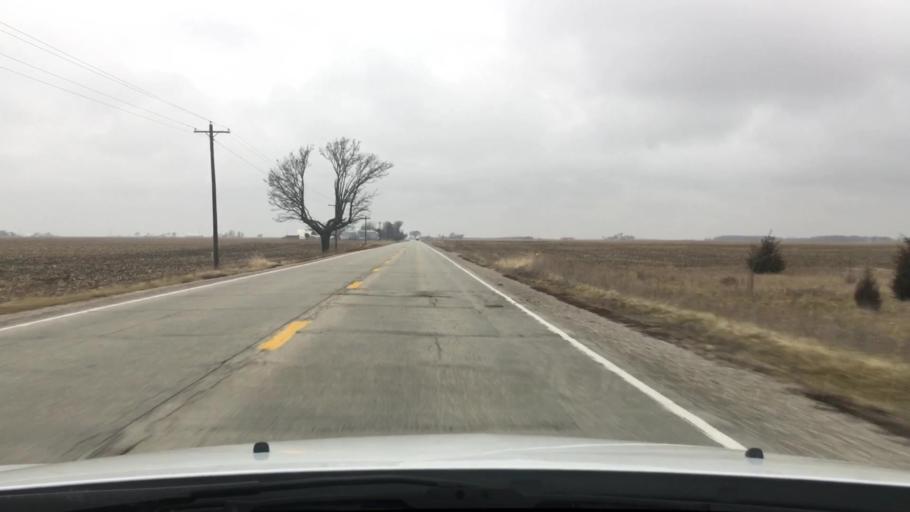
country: US
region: Illinois
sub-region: Iroquois County
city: Clifton
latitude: 40.8877
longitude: -87.8361
